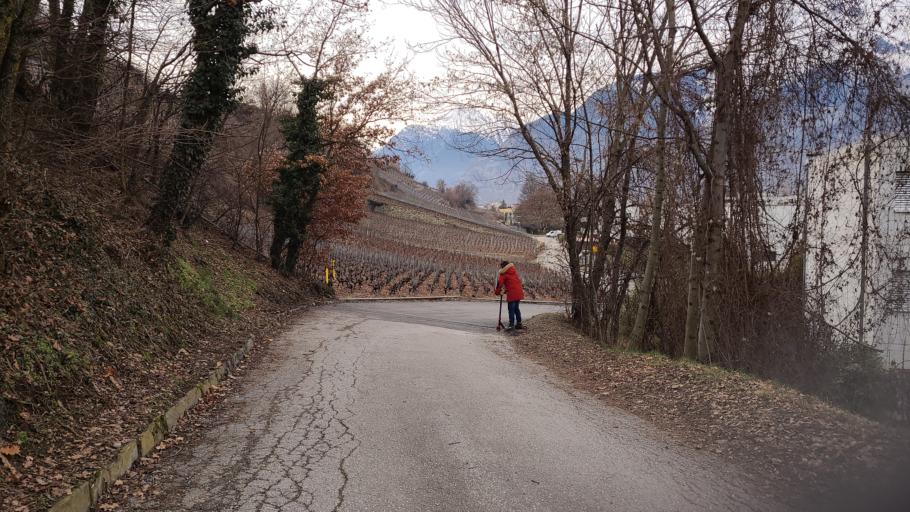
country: CH
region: Valais
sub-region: Conthey District
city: Conthey
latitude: 46.2219
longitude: 7.3142
